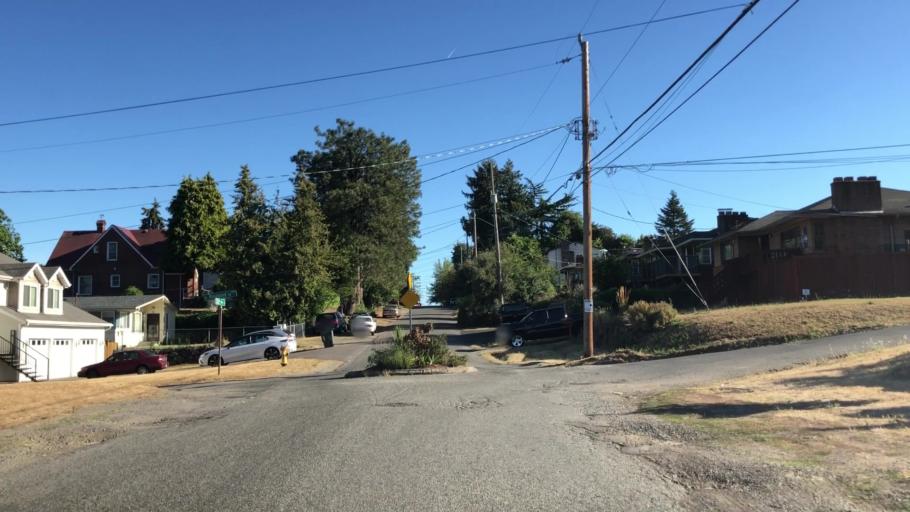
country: US
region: Washington
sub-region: King County
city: Boulevard Park
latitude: 47.5483
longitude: -122.2915
